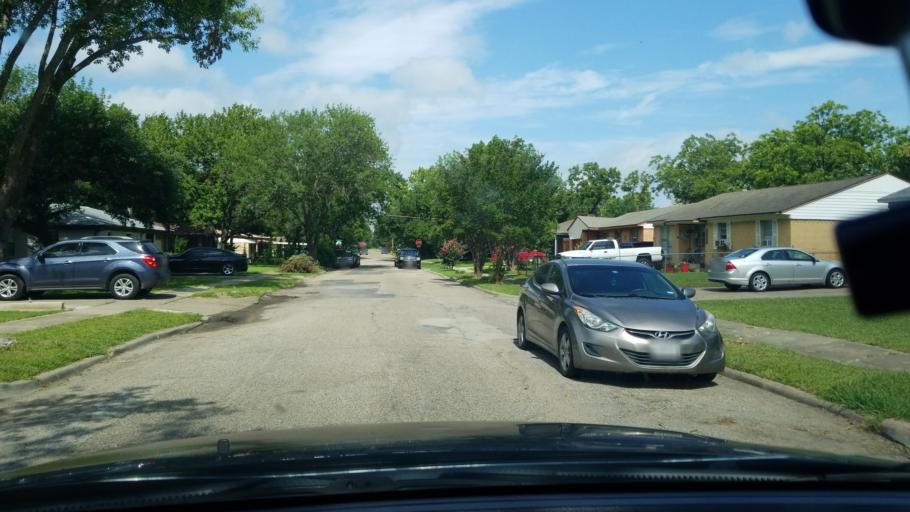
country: US
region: Texas
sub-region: Dallas County
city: Mesquite
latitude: 32.8198
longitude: -96.6524
